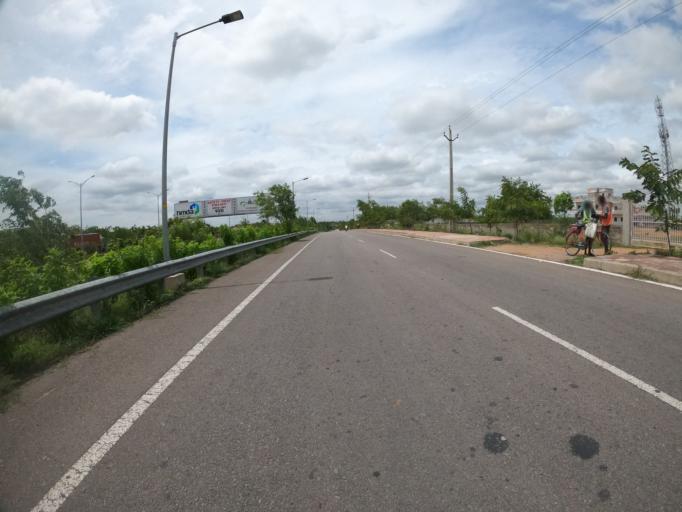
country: IN
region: Telangana
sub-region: Rangareddi
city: Balapur
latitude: 17.2887
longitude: 78.3816
